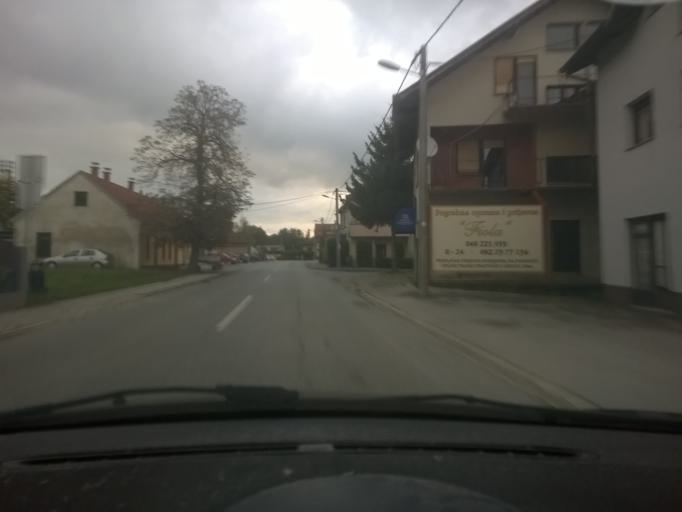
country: HR
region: Zagrebacka
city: Jakovlje
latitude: 45.9948
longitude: 15.8455
